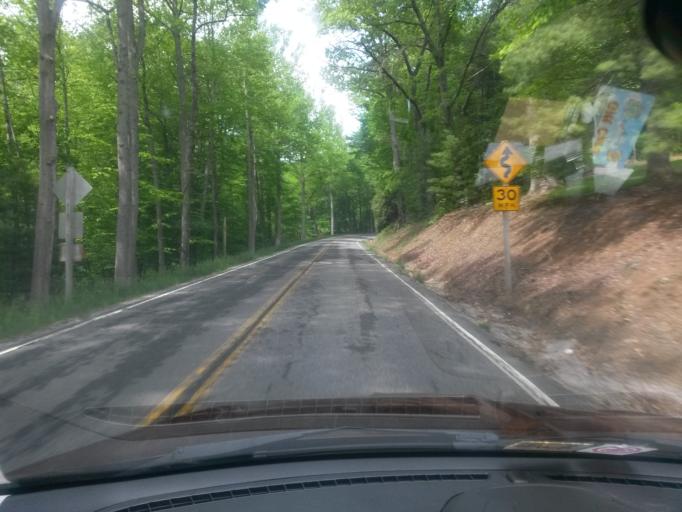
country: US
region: Virginia
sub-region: Floyd County
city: Floyd
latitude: 36.8957
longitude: -80.3227
